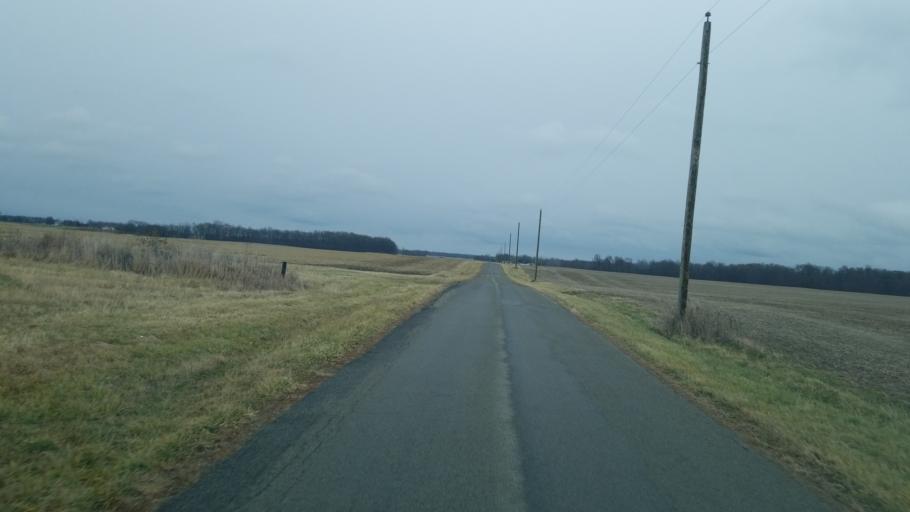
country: US
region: Ohio
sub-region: Union County
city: Marysville
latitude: 40.3091
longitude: -83.3137
